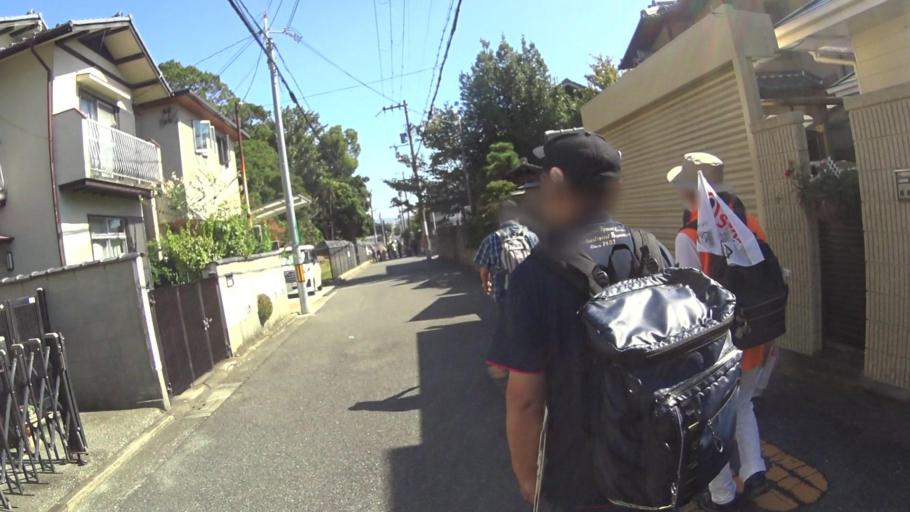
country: JP
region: Osaka
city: Takaishi
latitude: 34.5353
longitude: 135.4635
